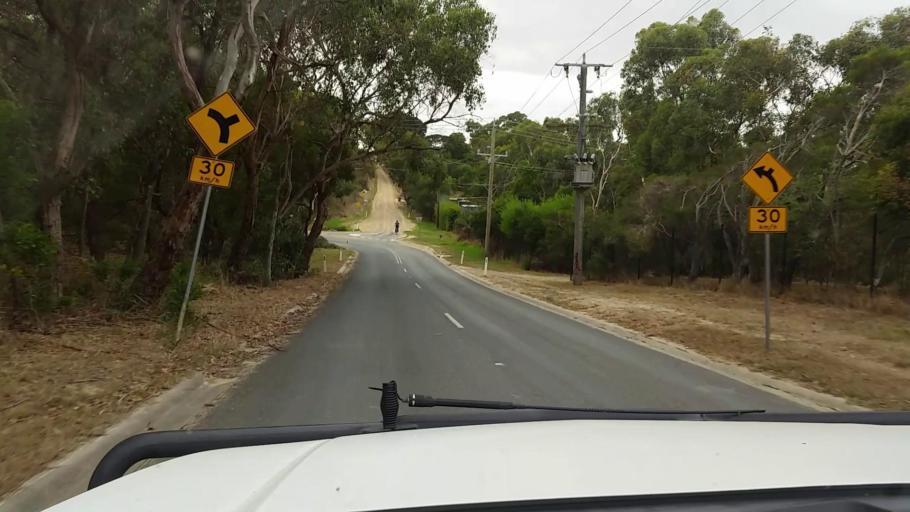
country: AU
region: Victoria
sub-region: Mornington Peninsula
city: Moorooduc
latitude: -38.2765
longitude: 145.0982
